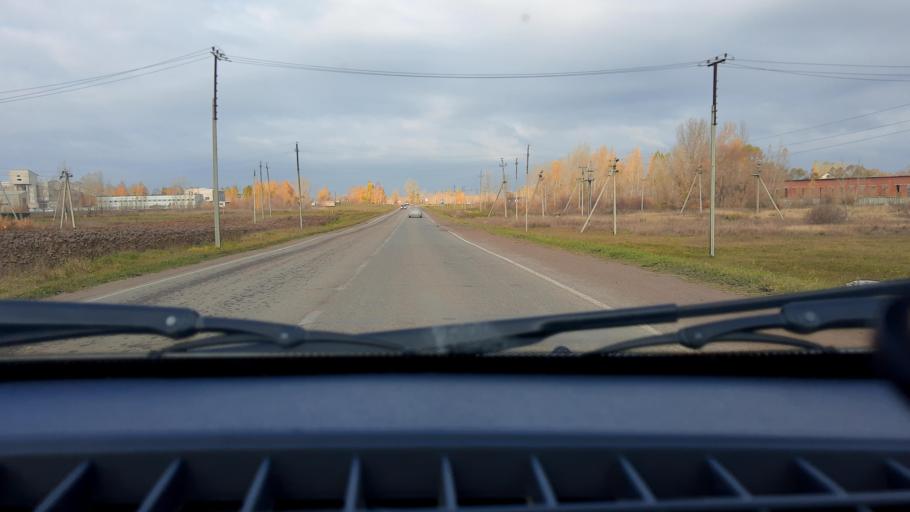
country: RU
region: Bashkortostan
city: Kabakovo
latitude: 54.5449
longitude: 56.1177
